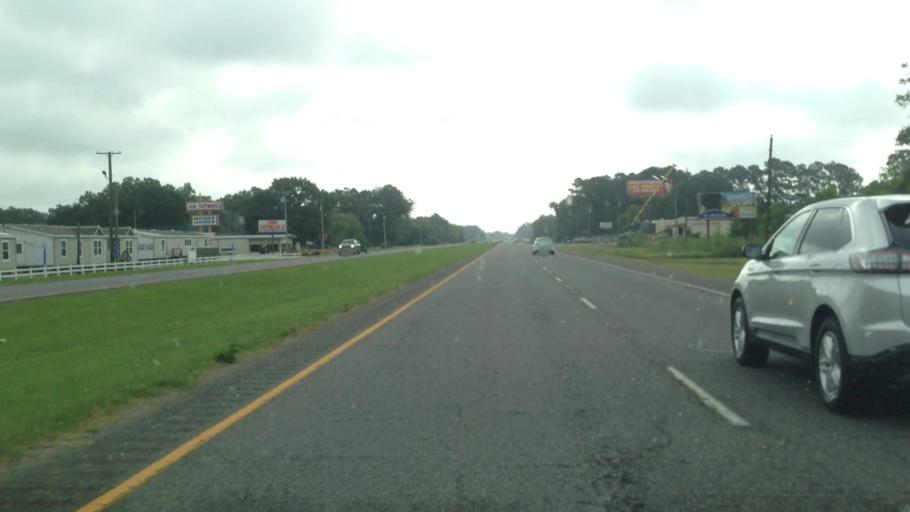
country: US
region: Louisiana
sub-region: Saint Landry Parish
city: Opelousas
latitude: 30.5412
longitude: -92.0254
